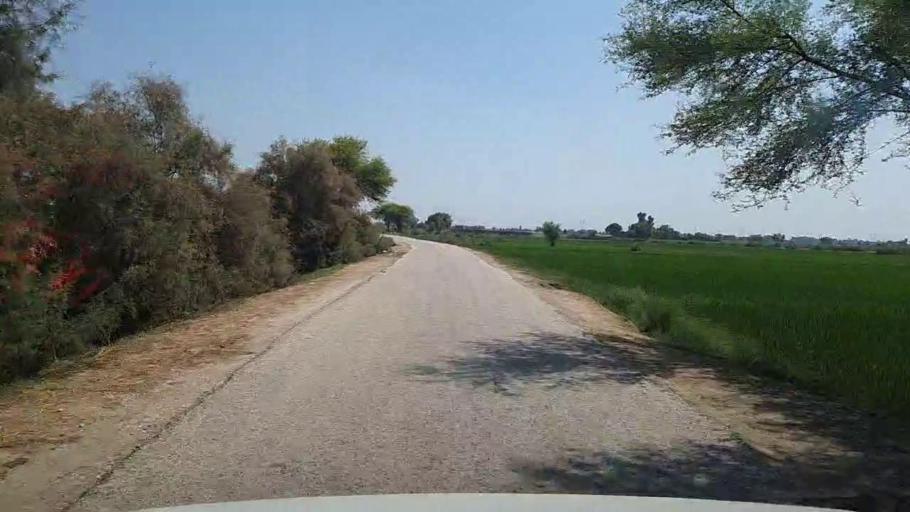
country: PK
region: Sindh
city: Kandhkot
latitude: 28.3147
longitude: 69.3402
